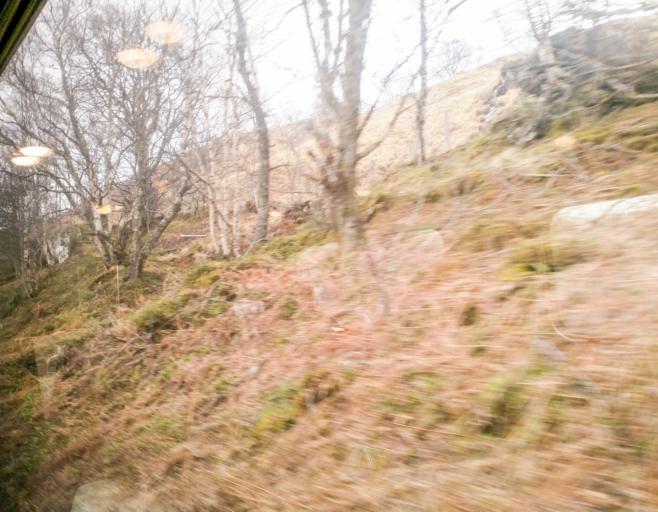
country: GB
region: Scotland
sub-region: Highland
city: Spean Bridge
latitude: 56.7879
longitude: -4.7294
